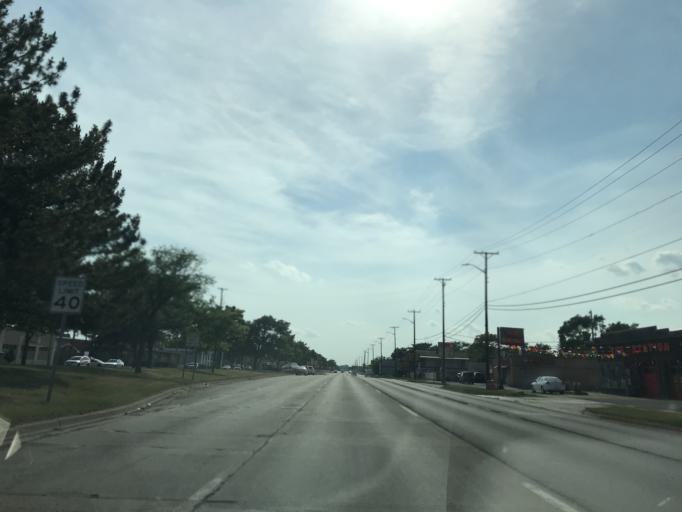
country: US
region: Michigan
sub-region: Wayne County
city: Inkster
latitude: 42.2970
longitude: -83.2915
